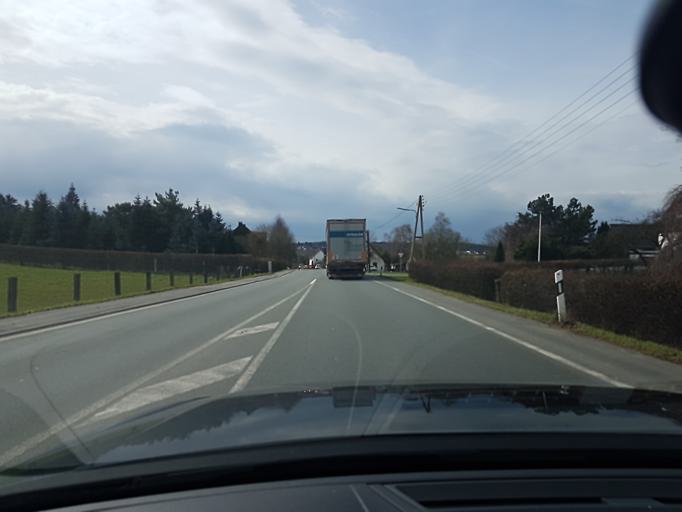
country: DE
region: North Rhine-Westphalia
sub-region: Regierungsbezirk Arnsberg
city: Holzwickede
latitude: 51.4493
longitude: 7.6778
